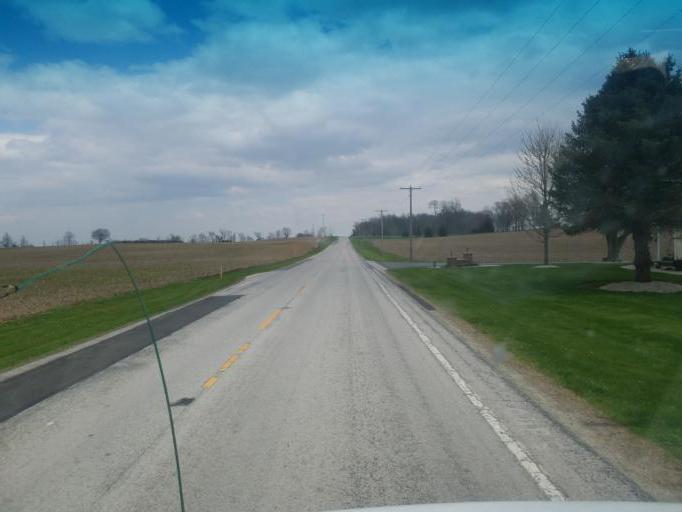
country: US
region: Ohio
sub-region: Wyandot County
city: Upper Sandusky
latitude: 40.9495
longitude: -83.2055
